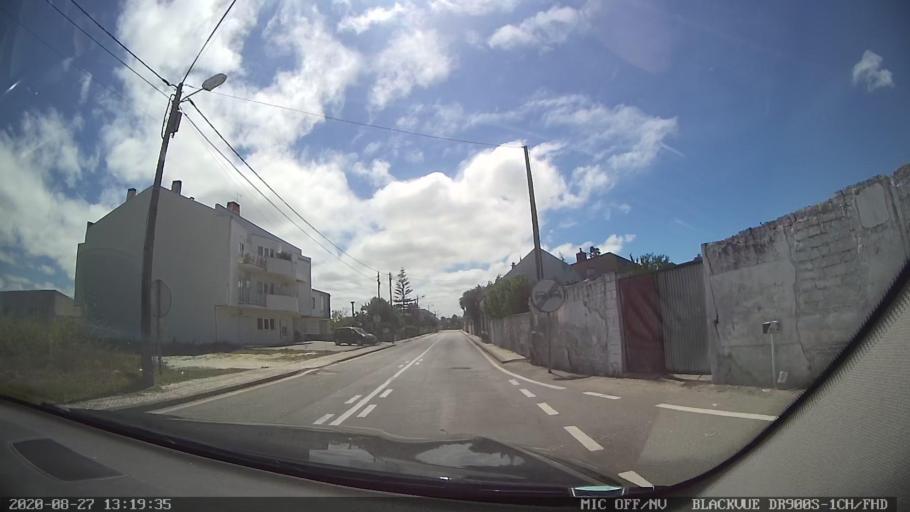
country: PT
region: Aveiro
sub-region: Vagos
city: Vagos
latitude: 40.5624
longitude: -8.6825
